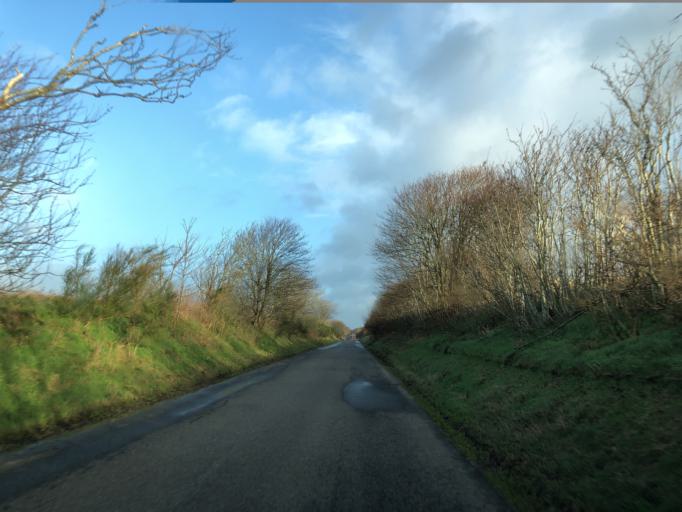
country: DK
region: Central Jutland
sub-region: Ringkobing-Skjern Kommune
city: Videbaek
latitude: 56.1963
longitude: 8.5491
